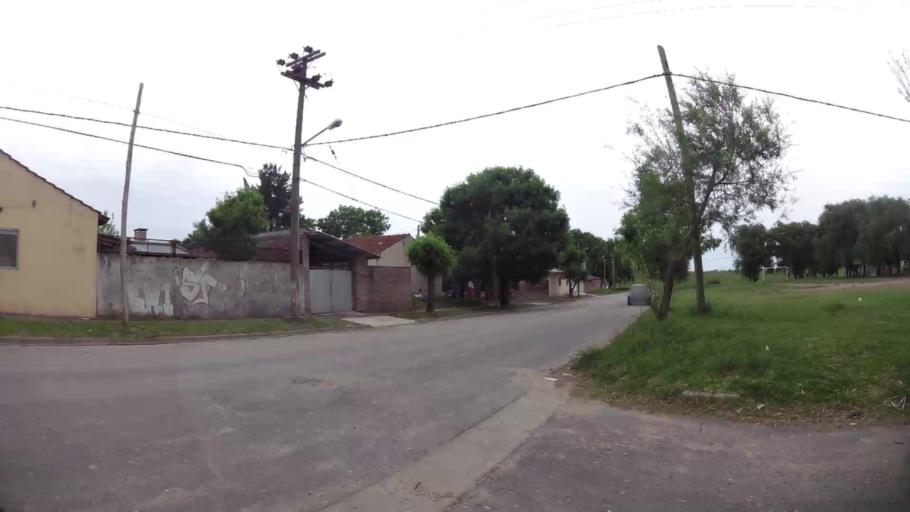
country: AR
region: Buenos Aires
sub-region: Partido de Campana
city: Campana
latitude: -34.2102
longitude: -58.9444
